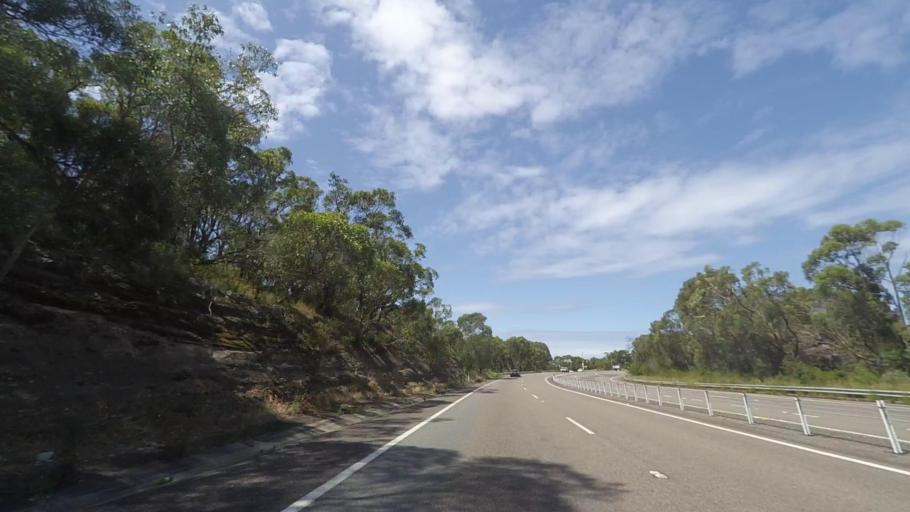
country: AU
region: New South Wales
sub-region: Wyong Shire
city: Kingfisher Shores
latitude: -33.1359
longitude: 151.6102
